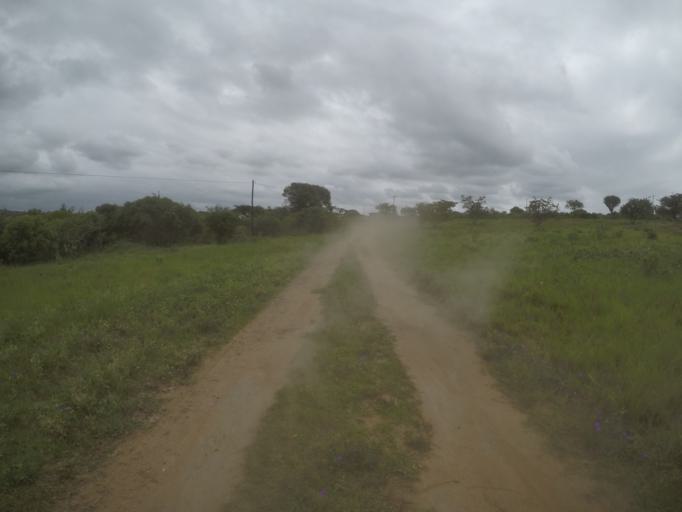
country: ZA
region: KwaZulu-Natal
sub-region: uThungulu District Municipality
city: Empangeni
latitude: -28.5937
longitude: 31.8449
